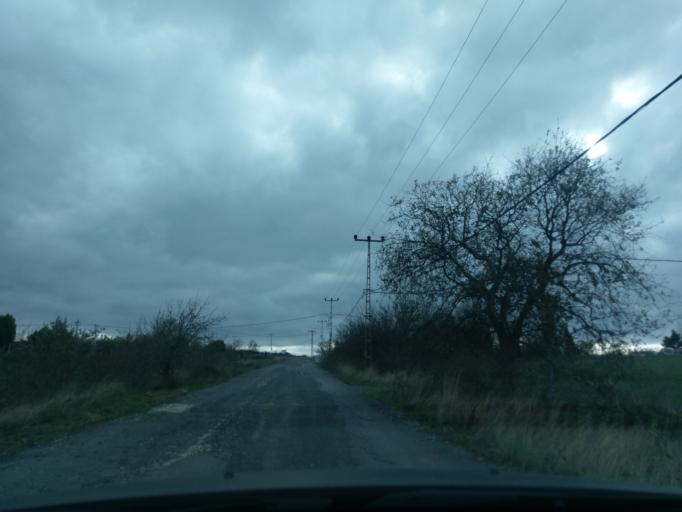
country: TR
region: Istanbul
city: Durusu
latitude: 41.2876
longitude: 28.6902
